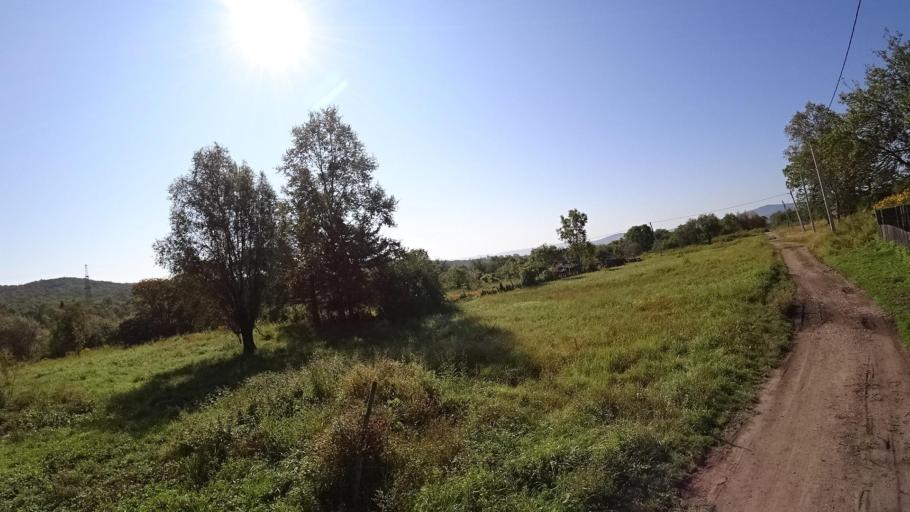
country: RU
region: Jewish Autonomous Oblast
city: Bira
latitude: 49.0084
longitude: 132.4758
